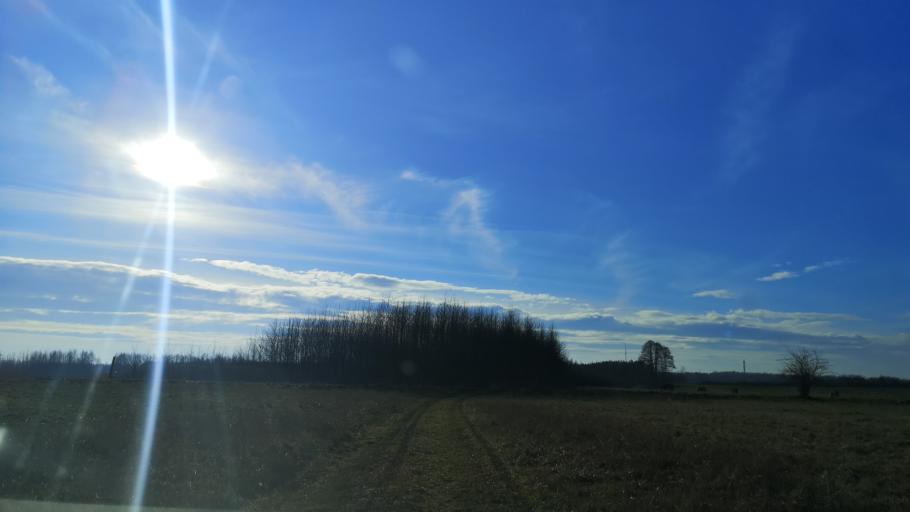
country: PL
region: Subcarpathian Voivodeship
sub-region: Powiat lezajski
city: Lezajsk
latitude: 50.2670
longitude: 22.4418
